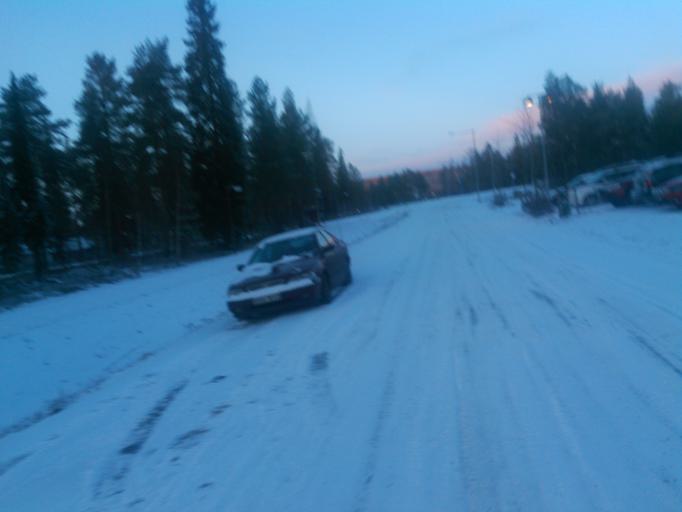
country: SE
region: Vaesterbotten
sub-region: Umea Kommun
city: Umea
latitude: 63.8192
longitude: 20.3182
